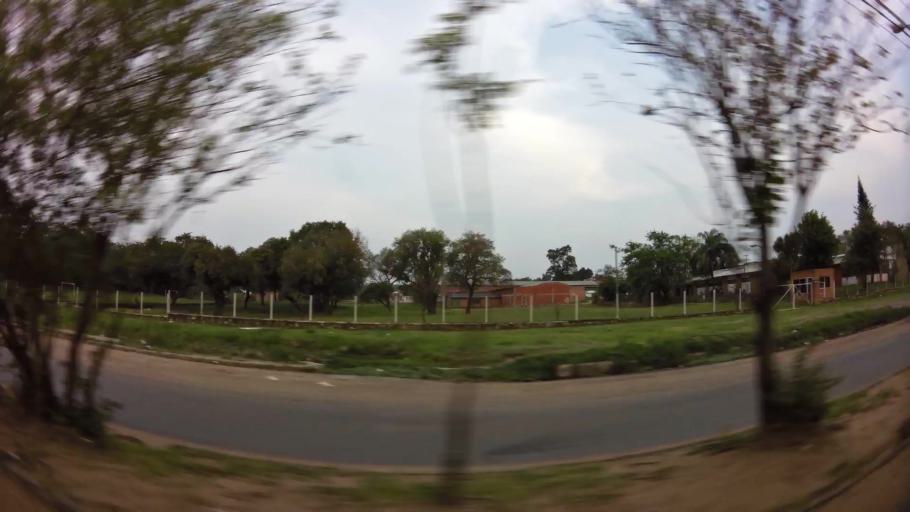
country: PY
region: Central
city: Lambare
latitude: -25.3522
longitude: -57.6418
